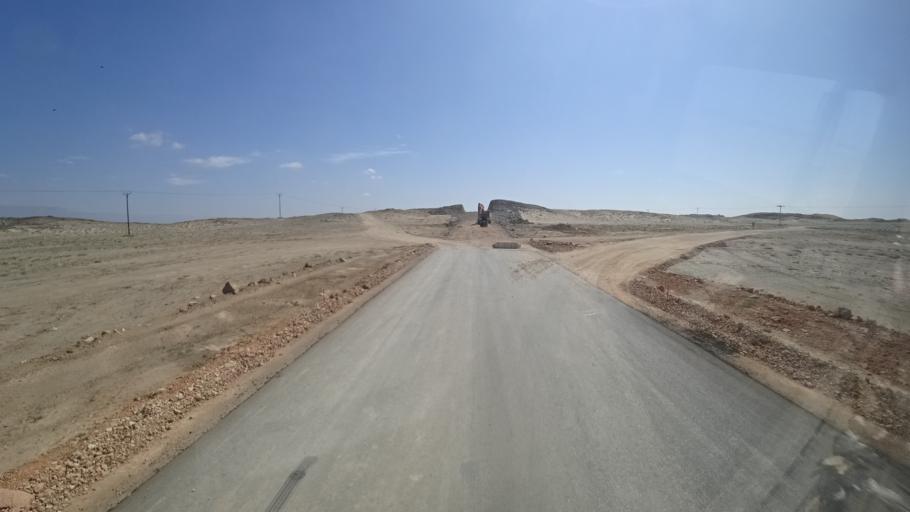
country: OM
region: Zufar
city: Salalah
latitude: 16.9644
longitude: 54.7665
